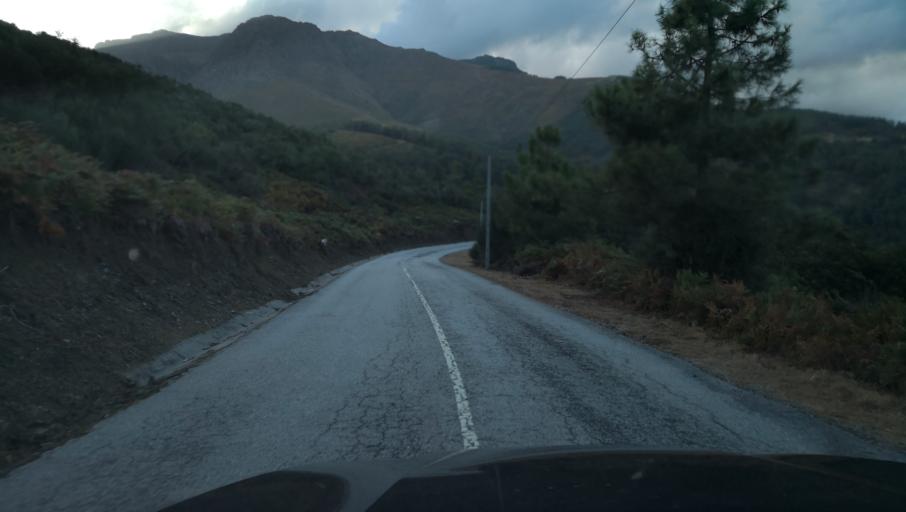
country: PT
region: Vila Real
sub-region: Santa Marta de Penaguiao
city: Santa Marta de Penaguiao
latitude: 41.2366
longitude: -7.8437
